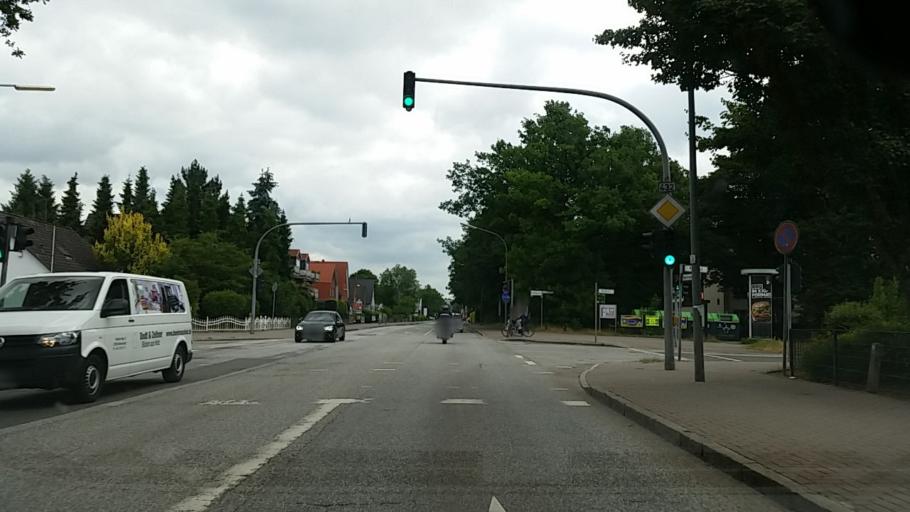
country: DE
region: Hamburg
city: Langenhorn
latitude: 53.6841
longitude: 10.0166
